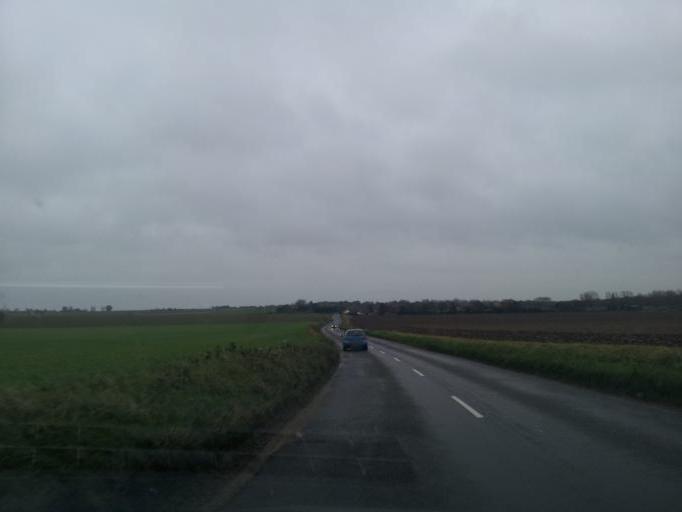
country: GB
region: England
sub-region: Norfolk
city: Hemsby
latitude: 52.7010
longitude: 1.6650
